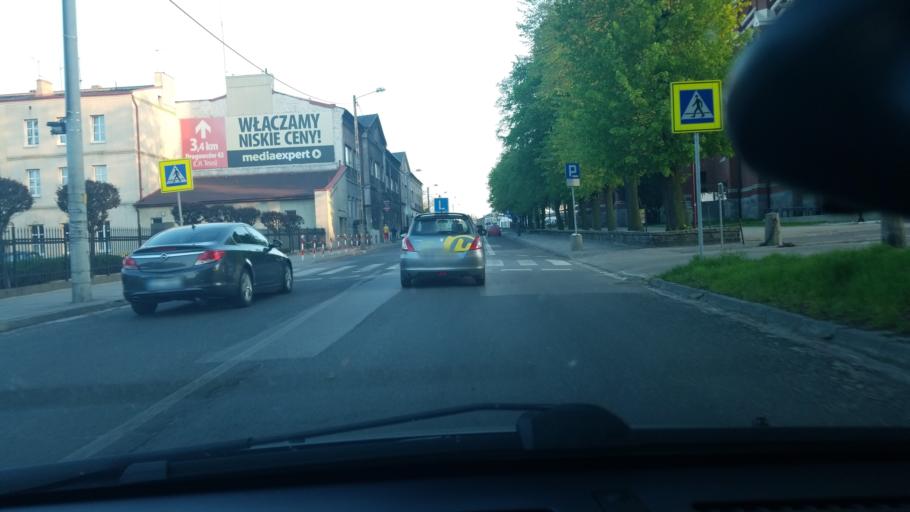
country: PL
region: Silesian Voivodeship
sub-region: Czestochowa
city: Czestochowa
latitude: 50.8093
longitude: 19.1278
